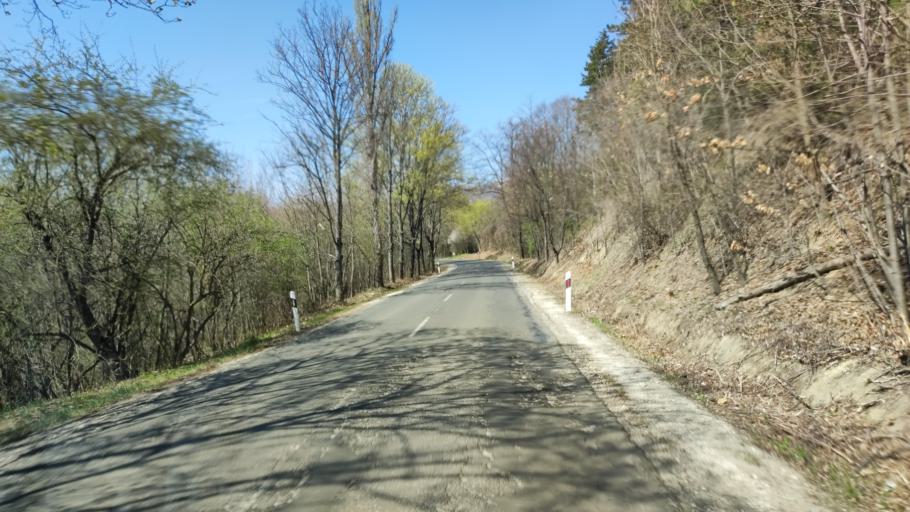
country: HU
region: Pest
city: Kosd
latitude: 47.7954
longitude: 19.1705
